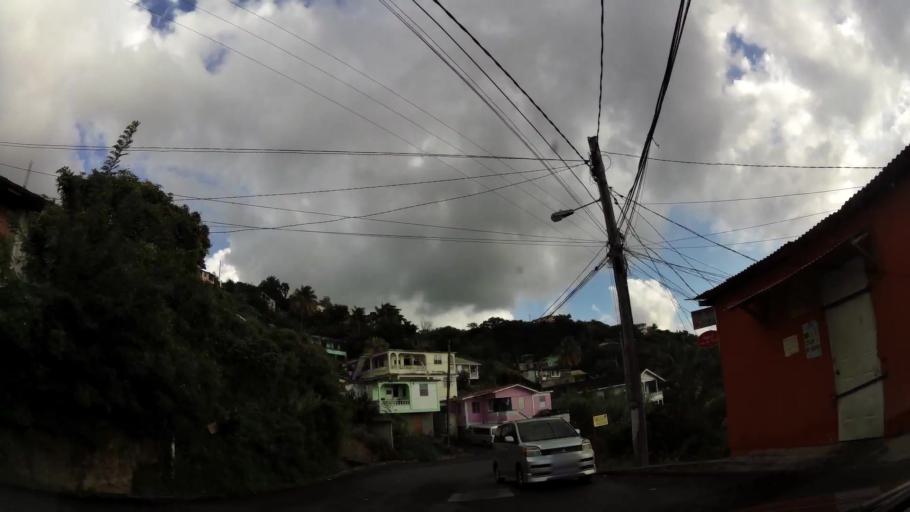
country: DM
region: Saint Paul
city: Mahaut
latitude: 15.3377
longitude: -61.3892
